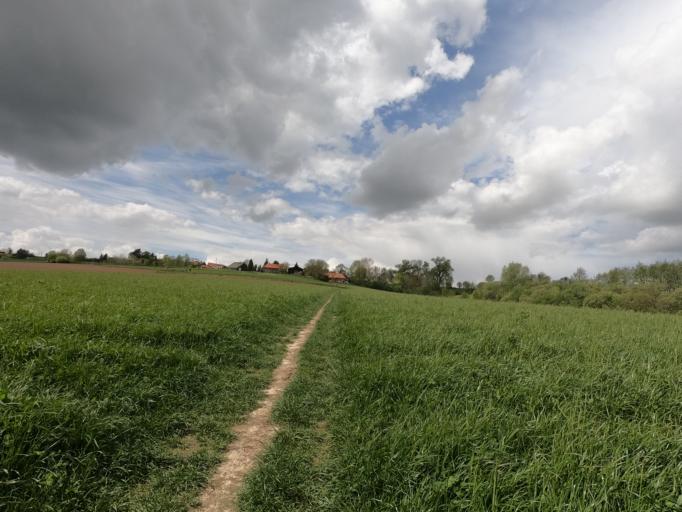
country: BE
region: Flanders
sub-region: Provincie Oost-Vlaanderen
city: Ronse
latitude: 50.7754
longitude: 3.5611
